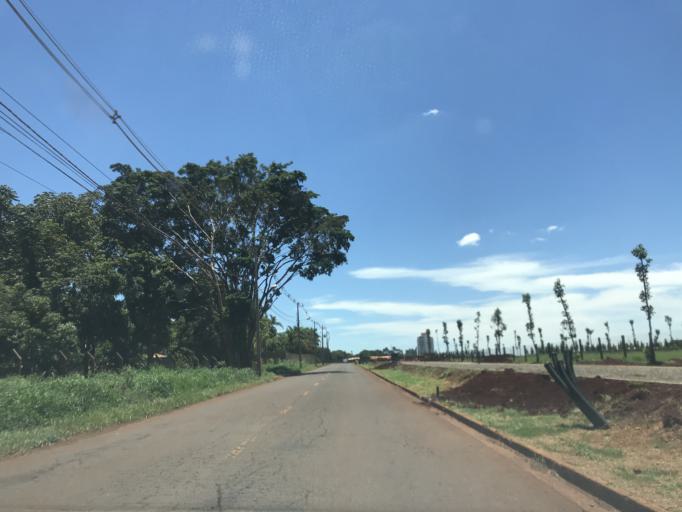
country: BR
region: Parana
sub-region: Sarandi
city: Sarandi
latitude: -23.4405
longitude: -51.9027
